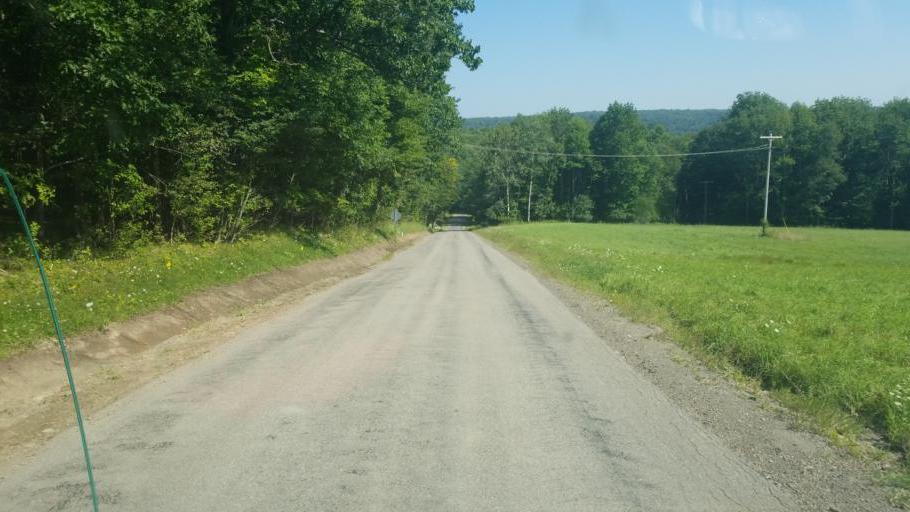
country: US
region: New York
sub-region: Allegany County
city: Bolivar
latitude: 42.0655
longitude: -78.0530
